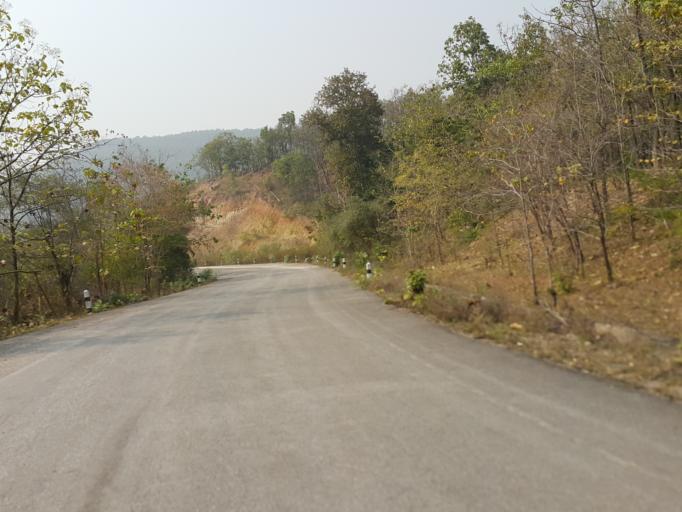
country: TH
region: Lampang
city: Mae Phrik
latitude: 17.5031
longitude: 99.0793
